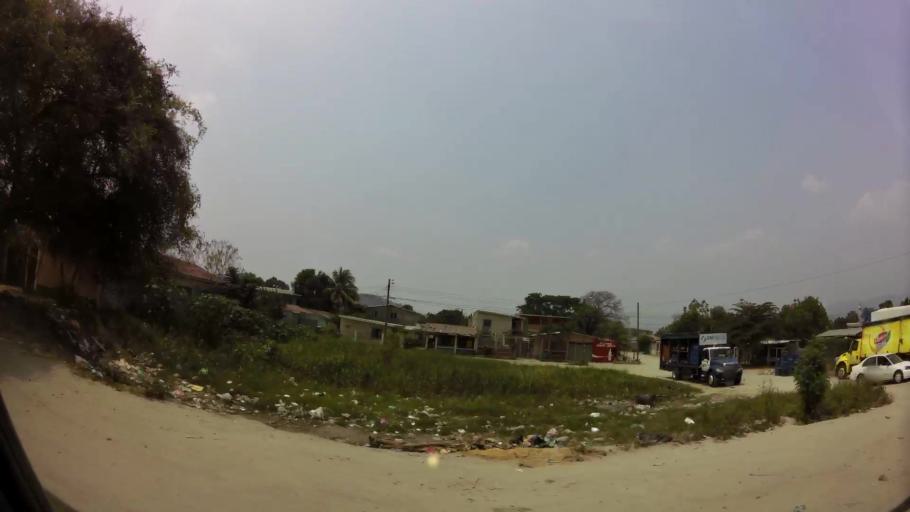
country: HN
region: Cortes
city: San Pedro Sula
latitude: 15.4775
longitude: -87.9897
